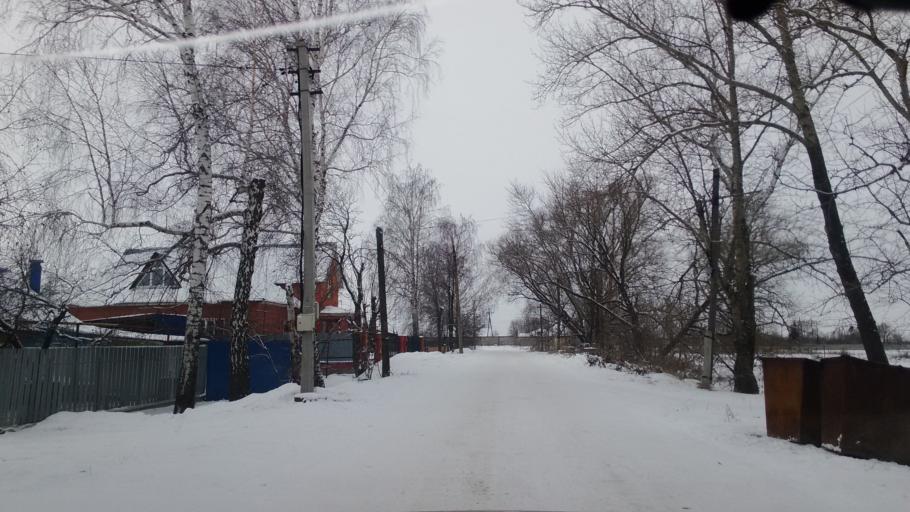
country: RU
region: Tula
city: Bogoroditsk
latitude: 53.7582
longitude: 38.1120
